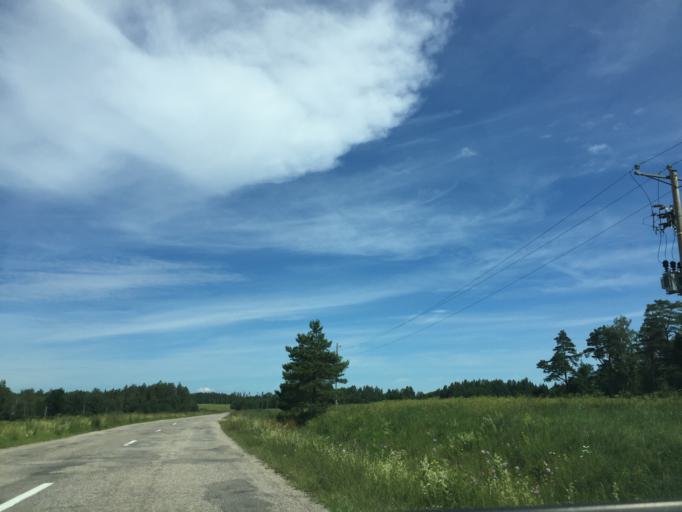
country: LV
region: Dundaga
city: Dundaga
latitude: 57.5478
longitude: 22.3211
